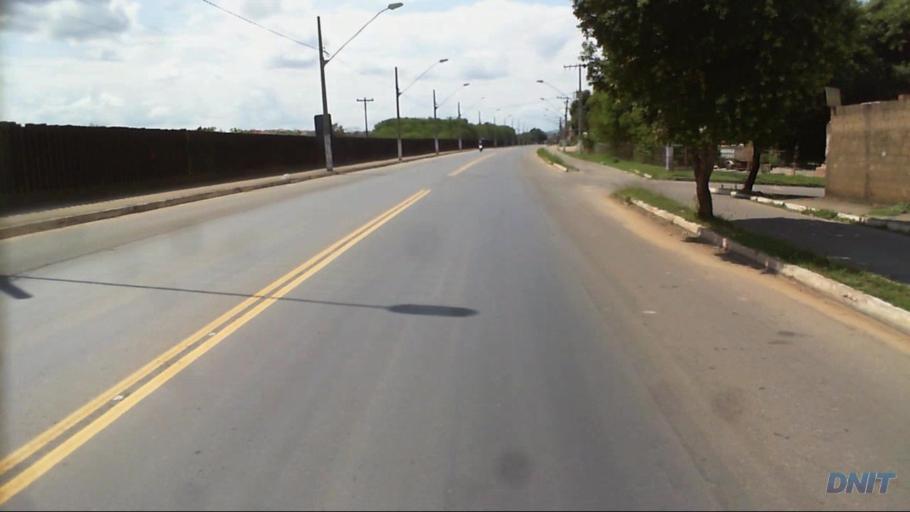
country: BR
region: Minas Gerais
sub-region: Governador Valadares
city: Governador Valadares
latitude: -18.8928
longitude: -41.9779
